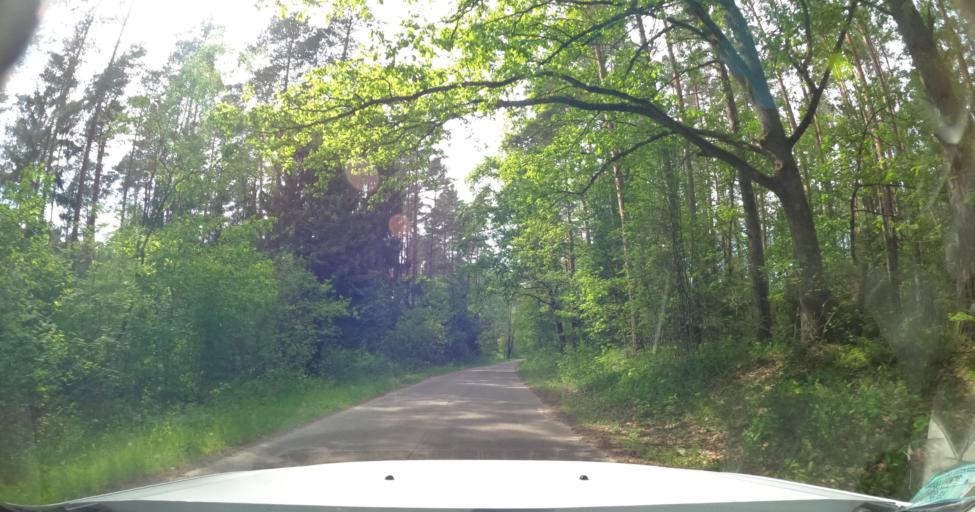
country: PL
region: Warmian-Masurian Voivodeship
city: Dobre Miasto
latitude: 54.0914
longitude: 20.4046
